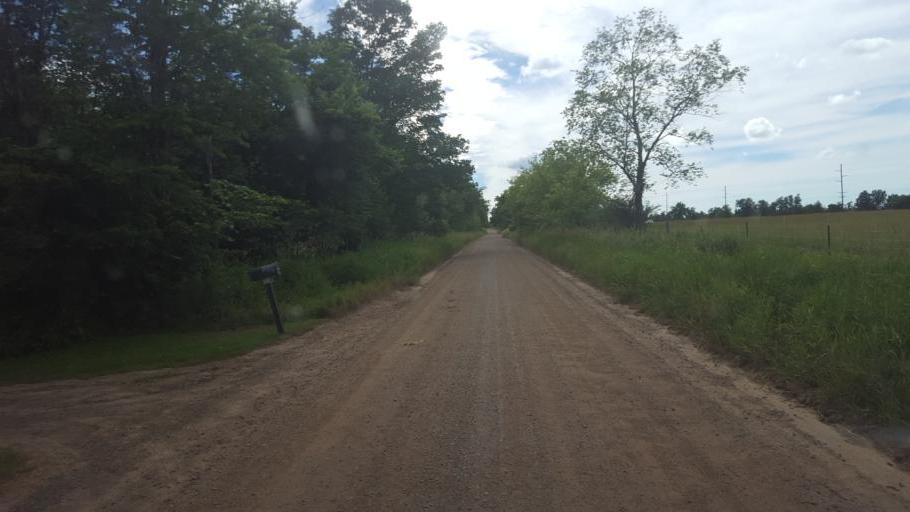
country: US
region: Michigan
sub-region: Barry County
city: Nashville
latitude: 42.5971
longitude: -84.9707
